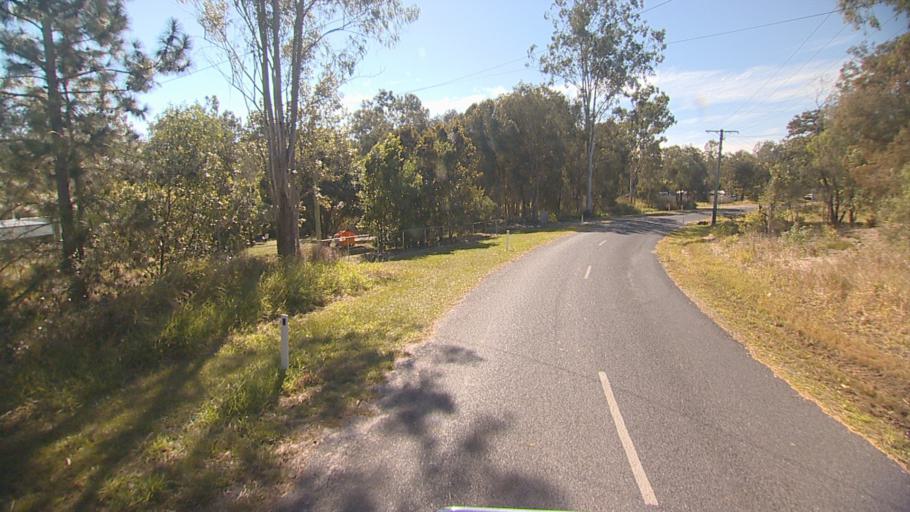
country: AU
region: Queensland
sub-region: Ipswich
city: Springfield Lakes
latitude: -27.7184
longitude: 152.9375
